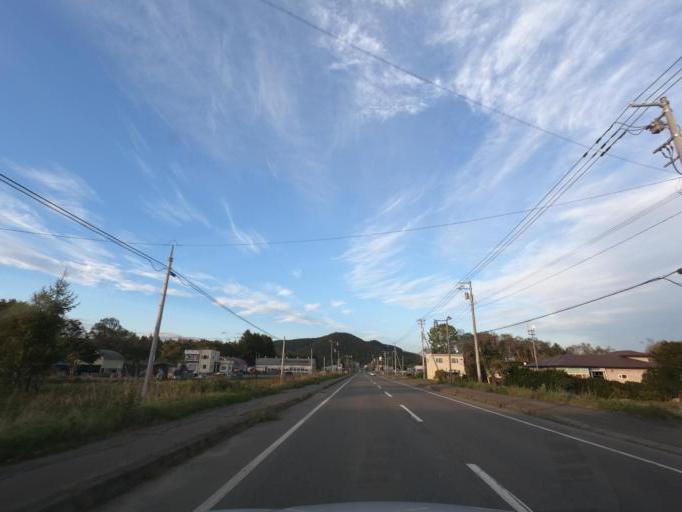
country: JP
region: Hokkaido
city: Obihiro
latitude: 42.5675
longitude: 143.3045
